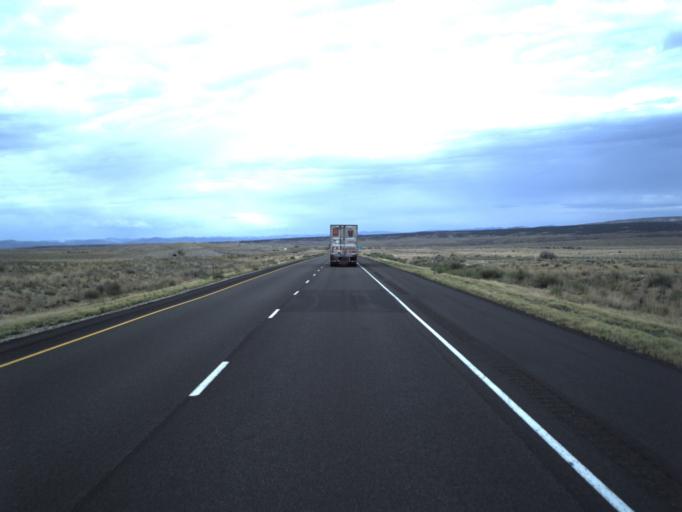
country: US
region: Colorado
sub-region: Mesa County
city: Loma
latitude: 39.0944
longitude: -109.2084
